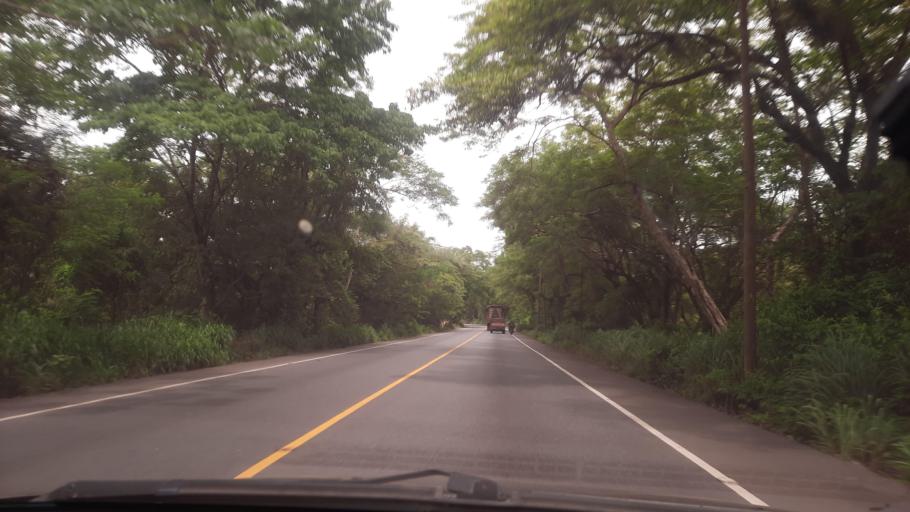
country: GT
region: Izabal
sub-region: Municipio de Los Amates
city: Los Amates
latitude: 15.2195
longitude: -89.2232
